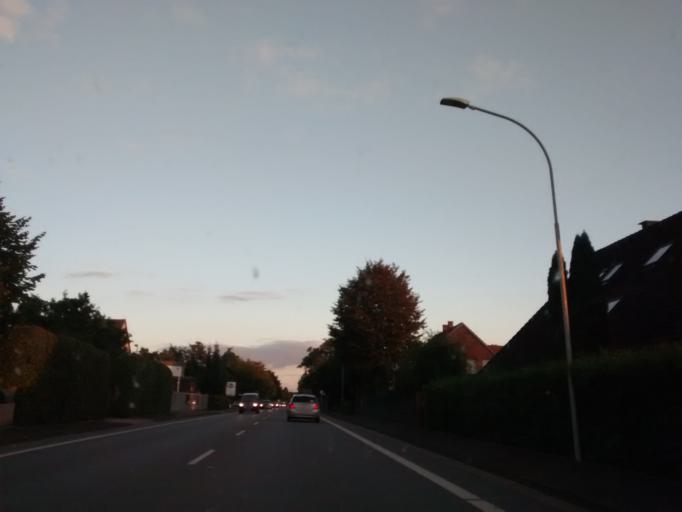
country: DE
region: North Rhine-Westphalia
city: Halle
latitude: 52.0523
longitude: 8.3753
